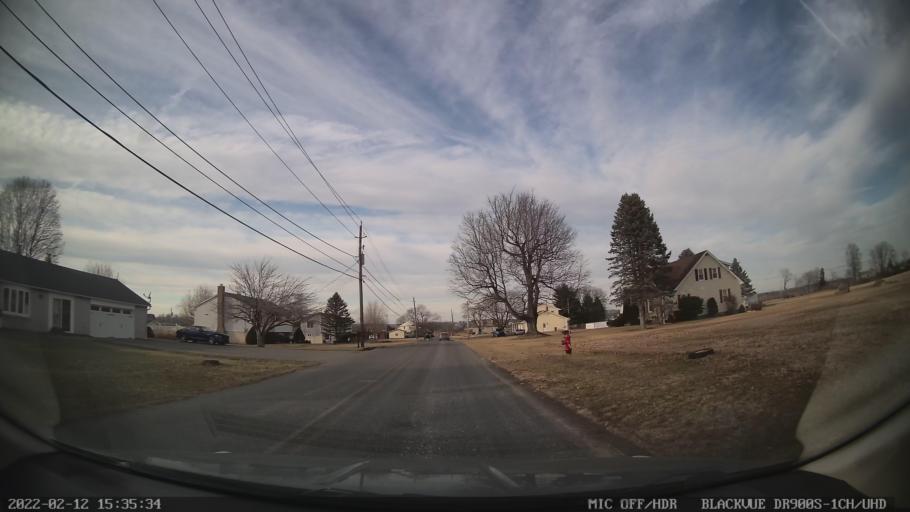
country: US
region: Pennsylvania
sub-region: Berks County
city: Topton
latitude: 40.4855
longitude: -75.7353
